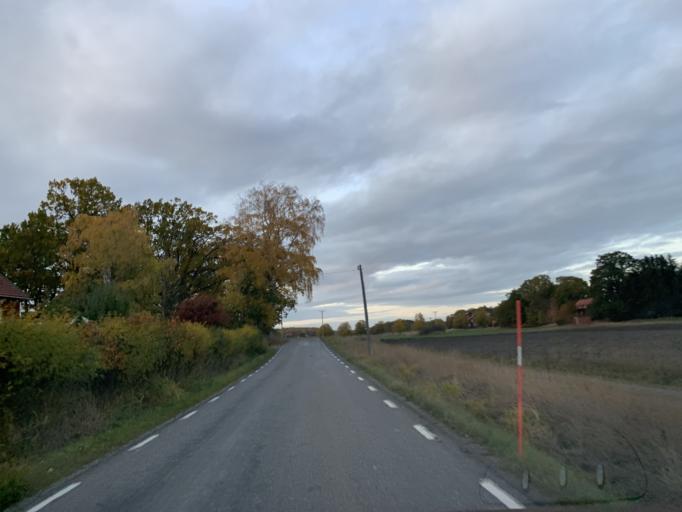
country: SE
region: Stockholm
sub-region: Nynashamns Kommun
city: Osmo
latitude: 58.9030
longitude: 17.7905
